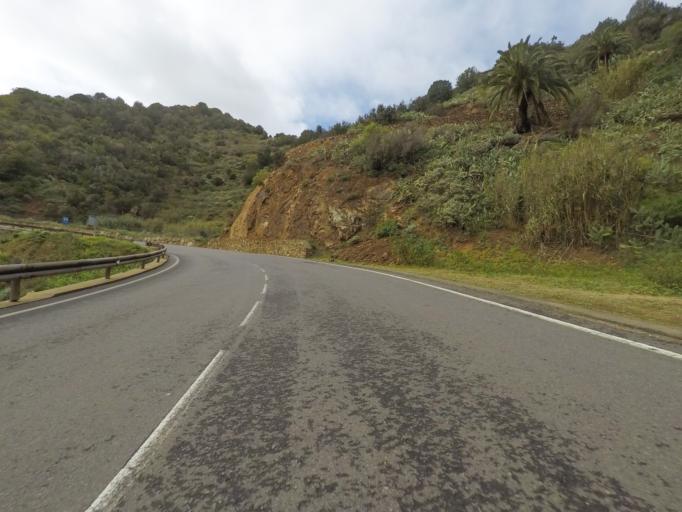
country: ES
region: Canary Islands
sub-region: Provincia de Santa Cruz de Tenerife
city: Vallehermosa
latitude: 28.1646
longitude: -17.2825
